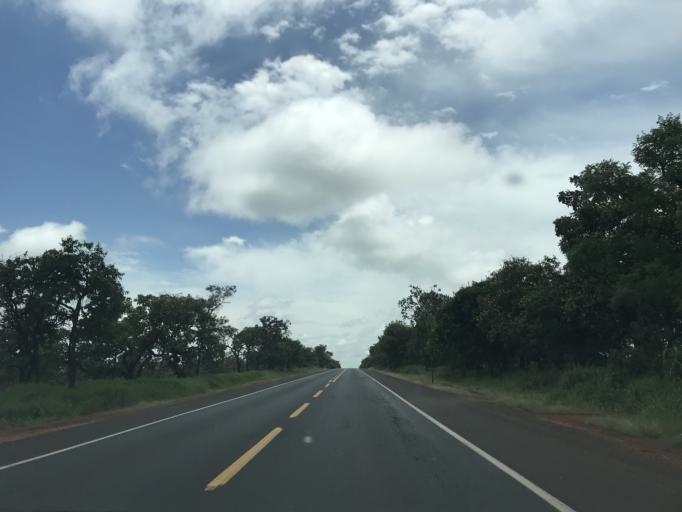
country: BR
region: Minas Gerais
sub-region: Prata
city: Prata
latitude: -19.6290
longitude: -48.9021
